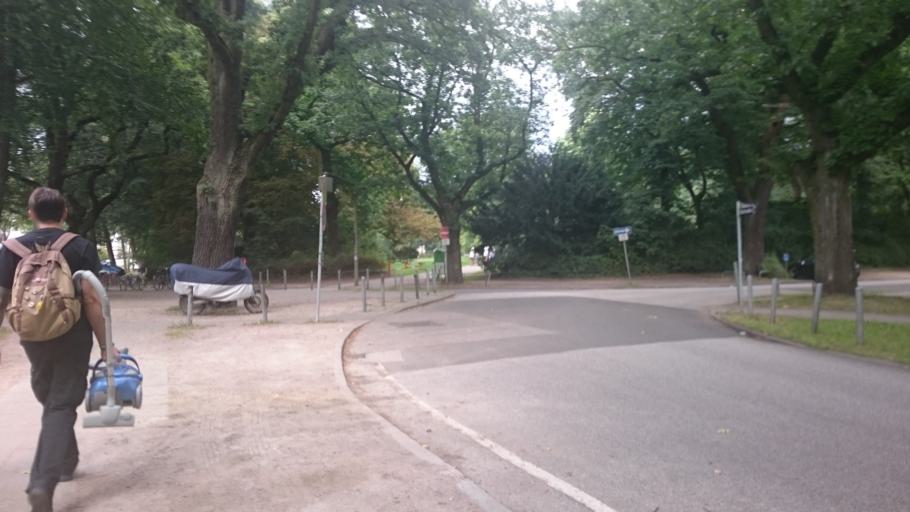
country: DE
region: Hamburg
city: Eimsbuettel
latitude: 53.5771
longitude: 9.9817
